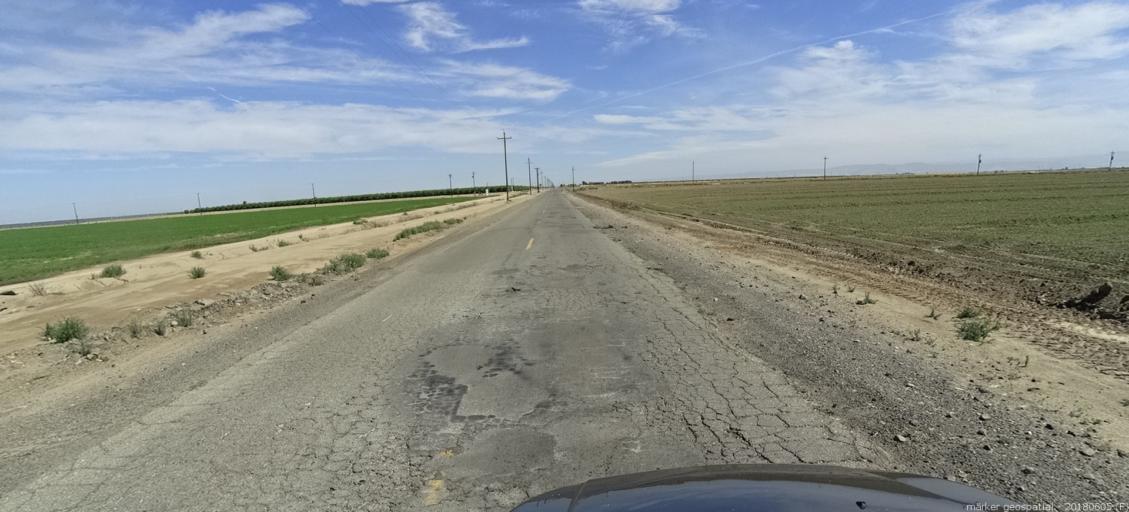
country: US
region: California
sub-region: Madera County
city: Chowchilla
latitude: 37.1247
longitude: -120.3828
